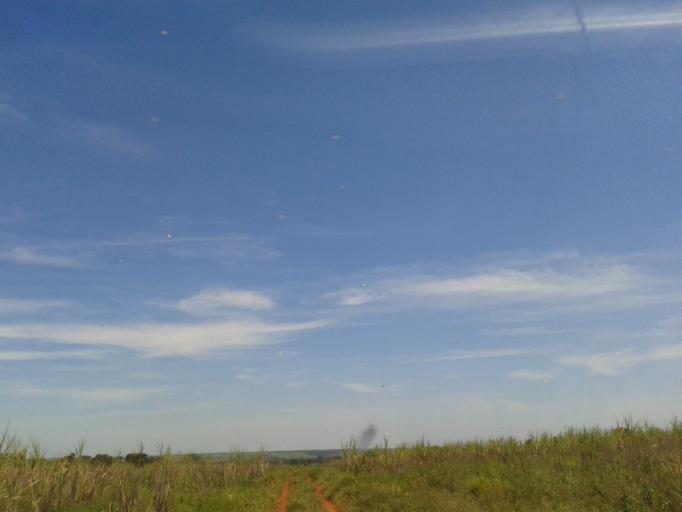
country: BR
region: Minas Gerais
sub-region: Santa Vitoria
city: Santa Vitoria
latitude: -19.1613
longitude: -50.5443
